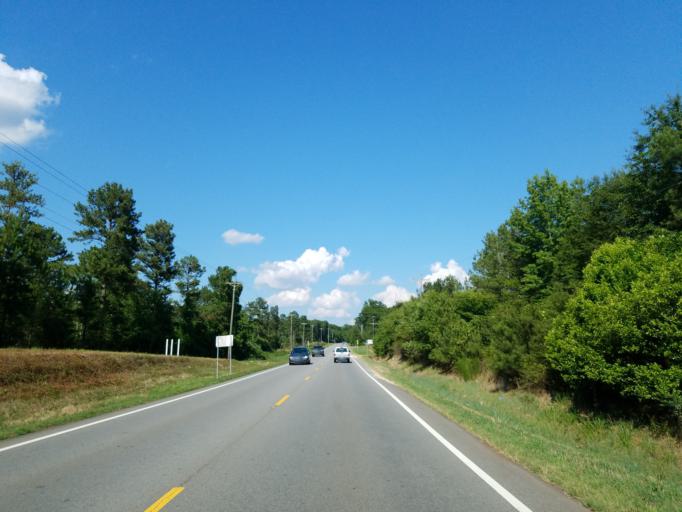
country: US
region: Georgia
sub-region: Peach County
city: Fort Valley
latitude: 32.5554
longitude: -83.8575
